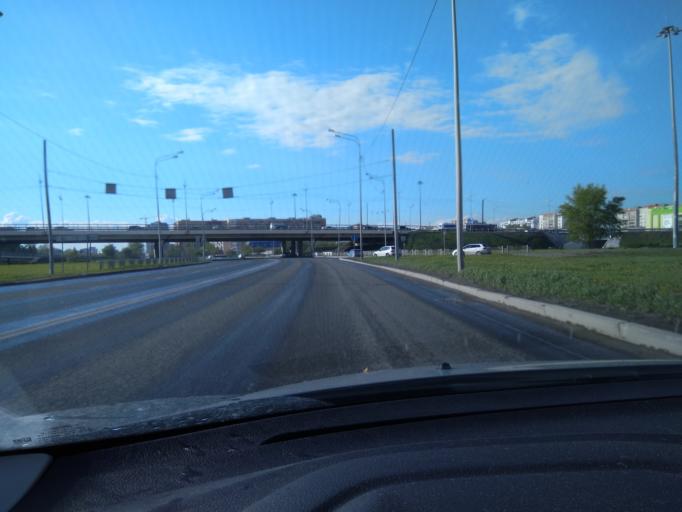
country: RU
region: Tjumen
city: Tyumen
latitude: 57.1423
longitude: 65.5398
